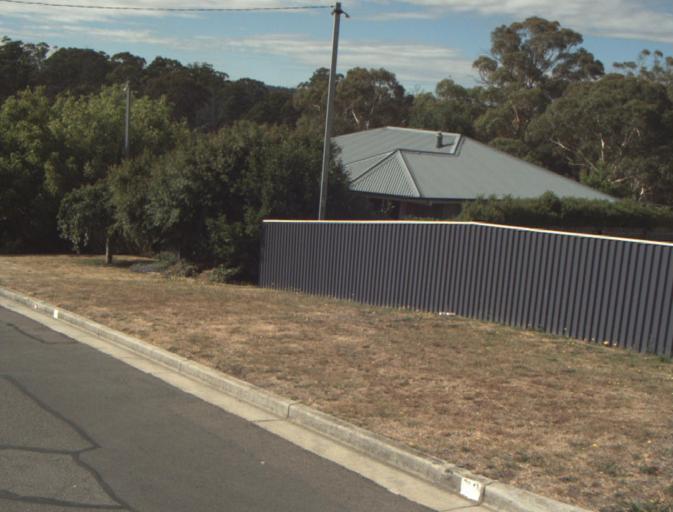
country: AU
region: Tasmania
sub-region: Launceston
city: Summerhill
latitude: -41.4687
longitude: 147.1158
